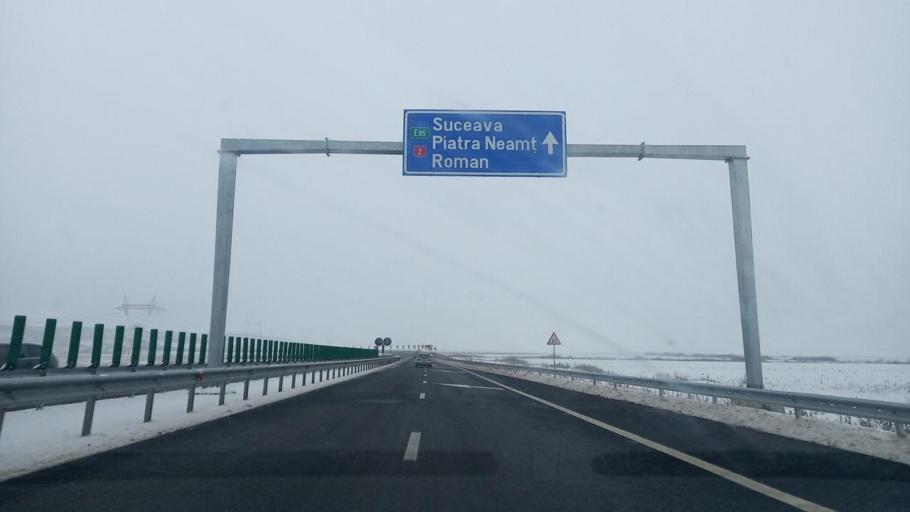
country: RO
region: Bacau
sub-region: Comuna Saucesti
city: Saucesti
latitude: 46.6348
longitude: 26.9347
